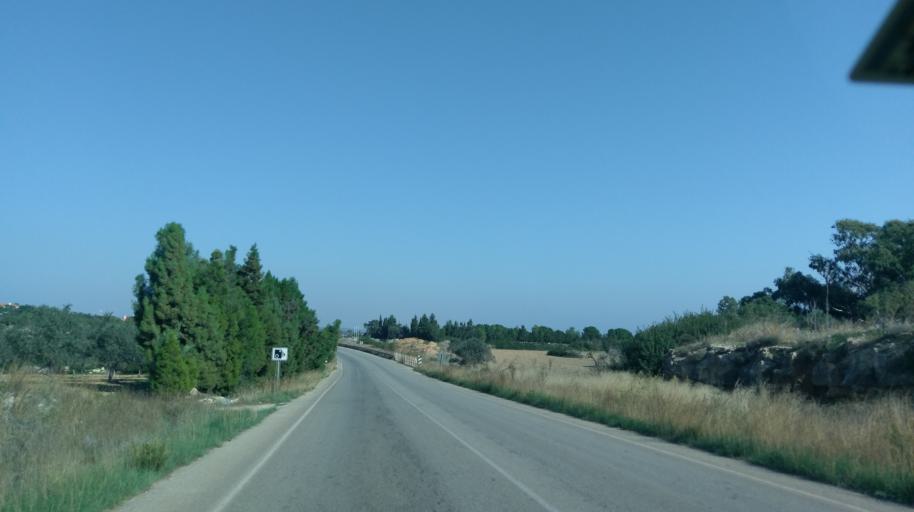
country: CY
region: Ammochostos
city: Leonarisso
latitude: 35.4186
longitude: 34.1229
